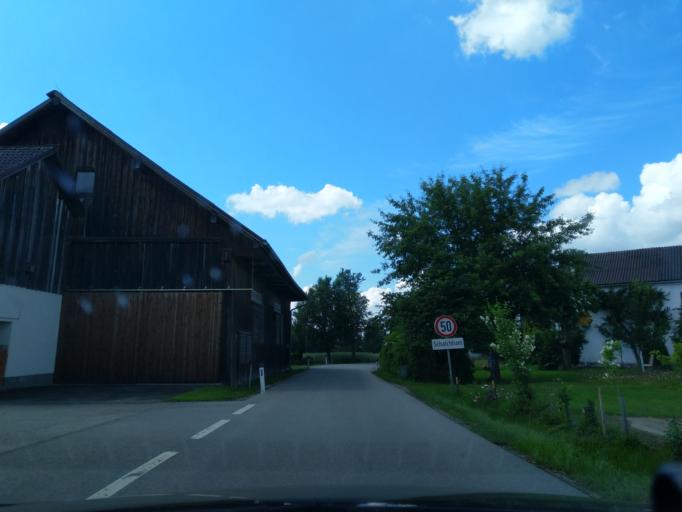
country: DE
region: Bavaria
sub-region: Lower Bavaria
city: Bad Fussing
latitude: 48.3124
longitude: 13.3610
